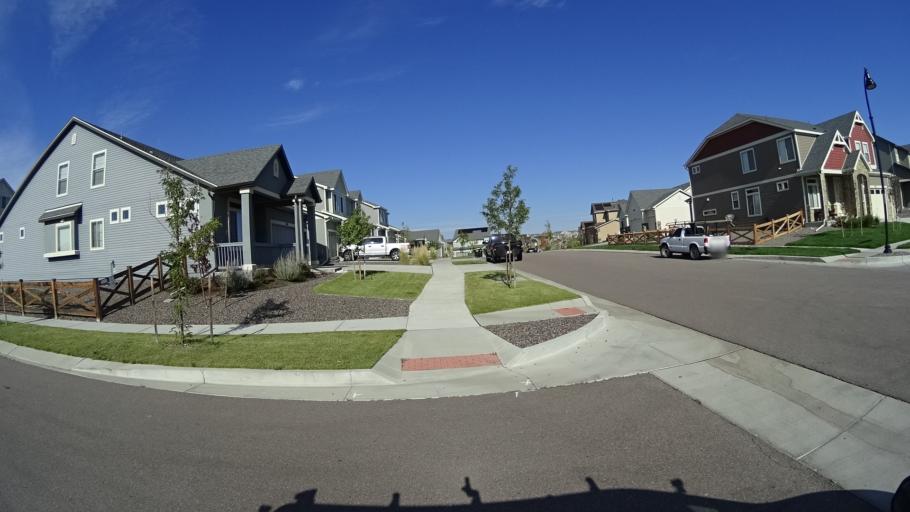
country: US
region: Colorado
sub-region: El Paso County
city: Cimarron Hills
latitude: 38.9285
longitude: -104.6644
